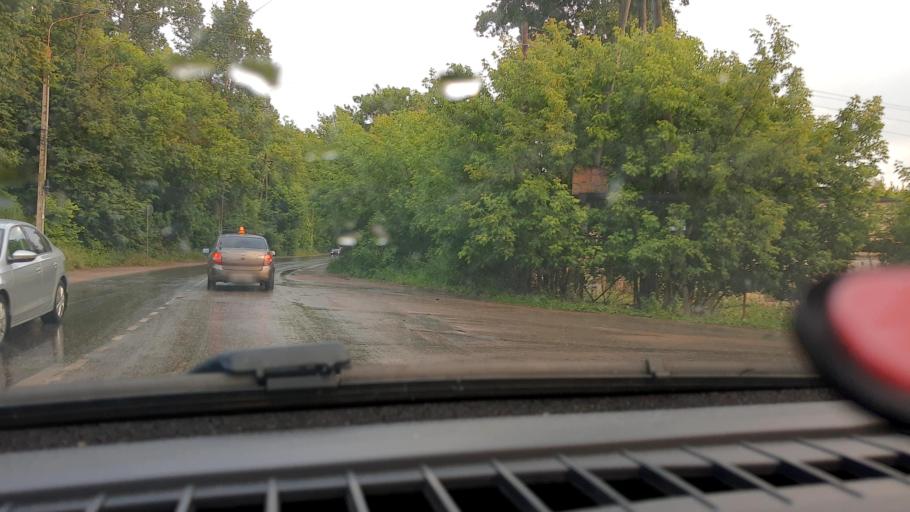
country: RU
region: Nizjnij Novgorod
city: Gorodets
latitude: 56.6502
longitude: 43.4652
